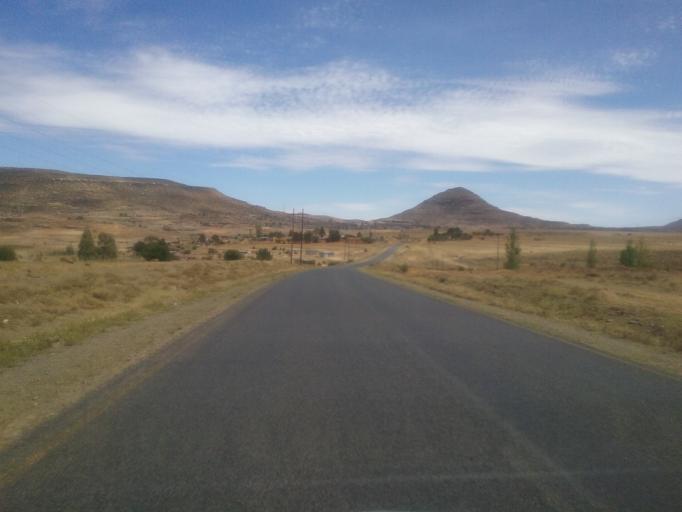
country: LS
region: Mafeteng
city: Mafeteng
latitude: -29.9699
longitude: 27.3081
